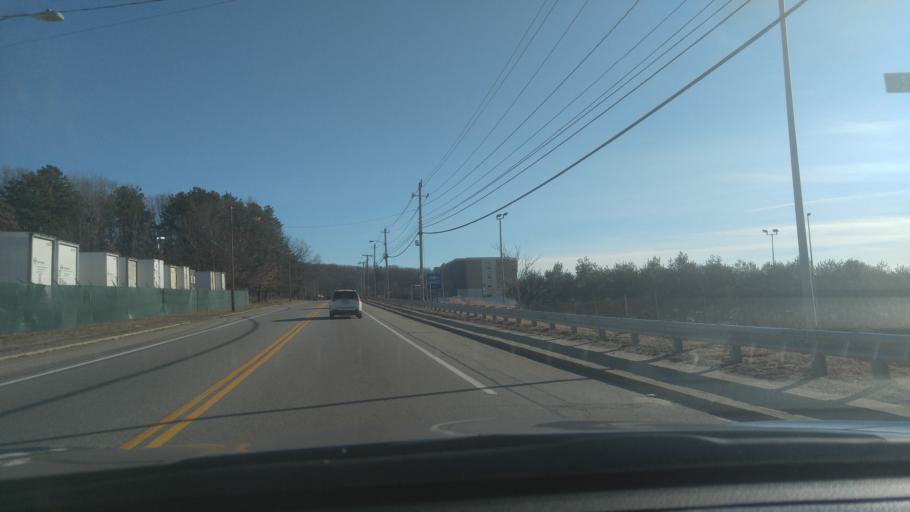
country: US
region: Rhode Island
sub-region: Providence County
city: Cumberland Hill
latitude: 41.9939
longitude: -71.4863
